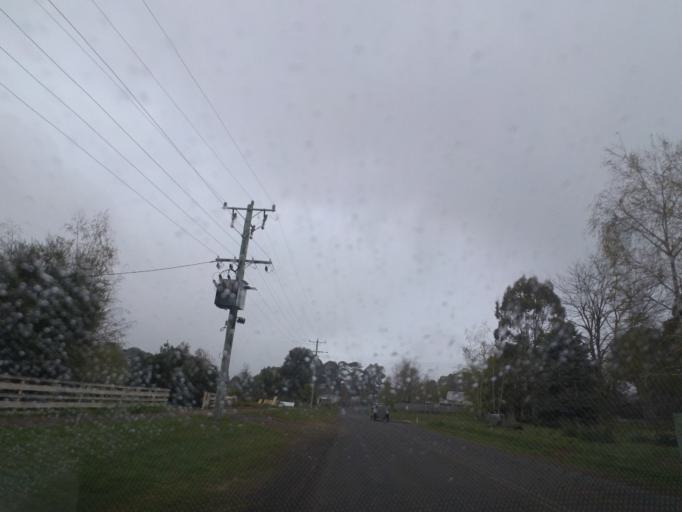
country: AU
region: Victoria
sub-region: Moorabool
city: Bacchus Marsh
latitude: -37.3849
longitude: 144.3161
